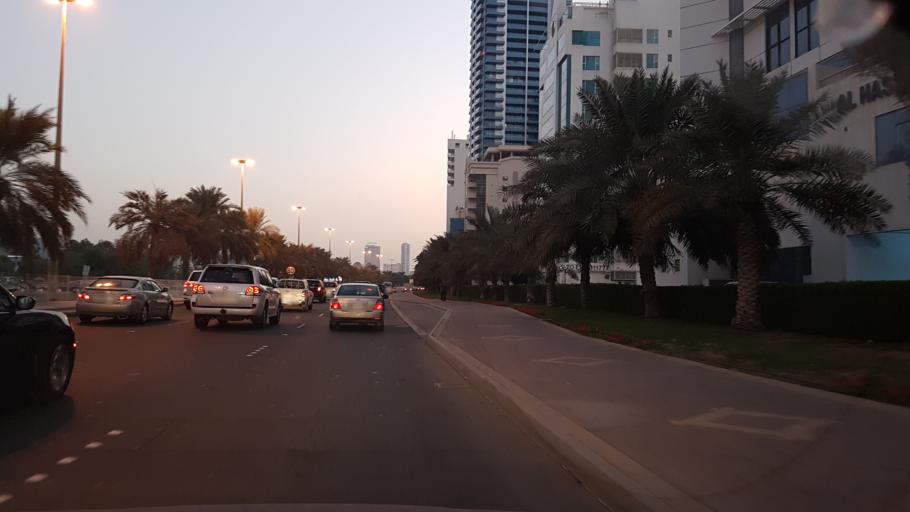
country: BH
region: Manama
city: Manama
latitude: 26.2305
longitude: 50.5986
